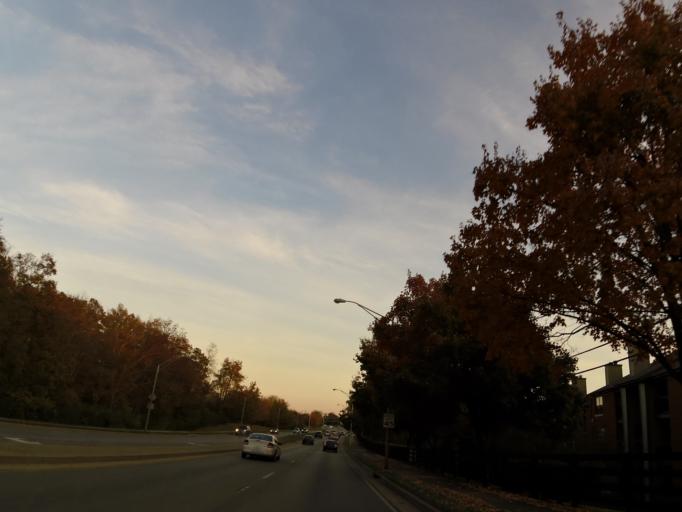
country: US
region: Kentucky
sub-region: Fayette County
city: Lexington
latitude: 37.9675
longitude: -84.4874
